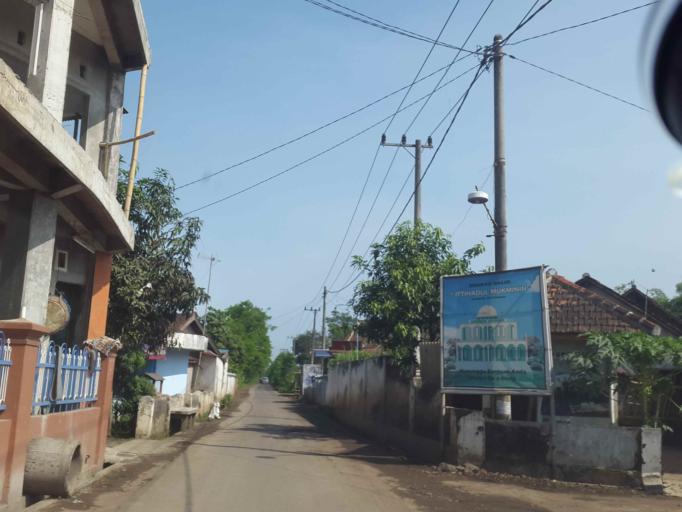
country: ID
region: East Java
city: Singosari
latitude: -7.9339
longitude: 112.6952
